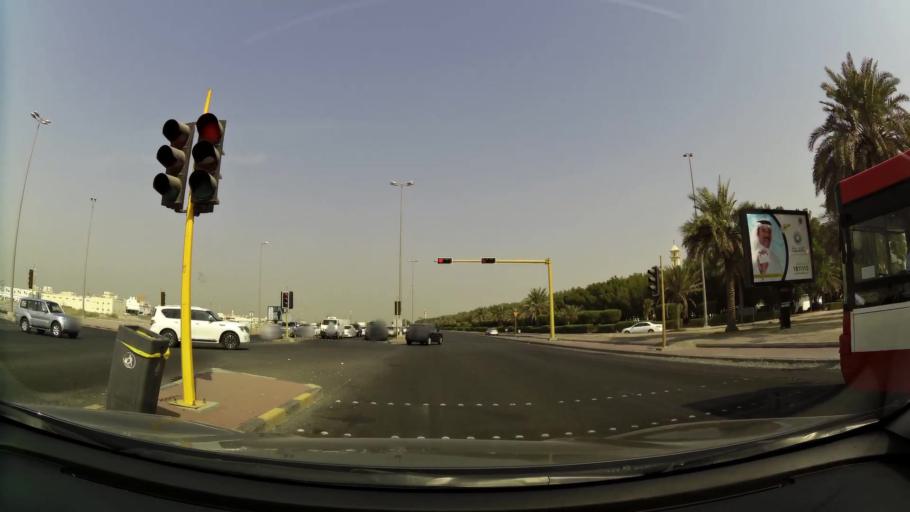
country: KW
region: Al Asimah
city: Ar Rabiyah
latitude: 29.2883
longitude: 47.9283
